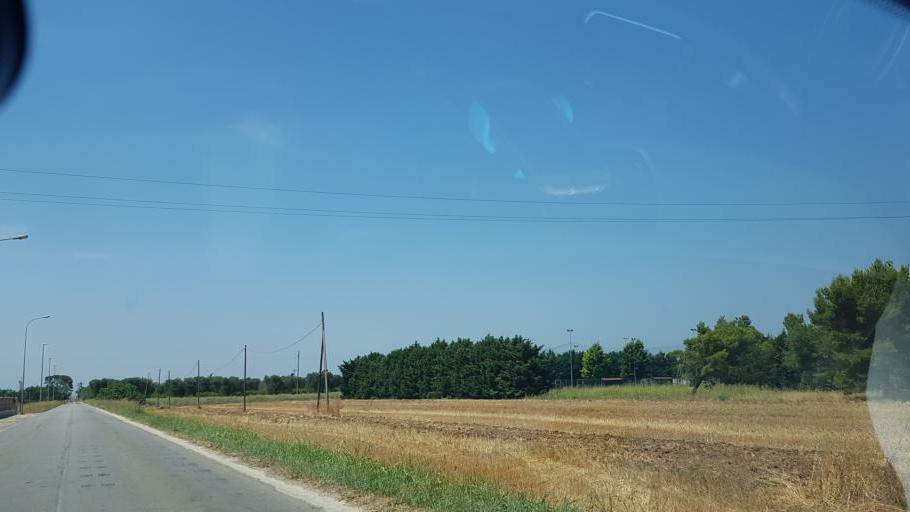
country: IT
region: Apulia
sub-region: Provincia di Brindisi
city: Mesagne
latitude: 40.5453
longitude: 17.8220
